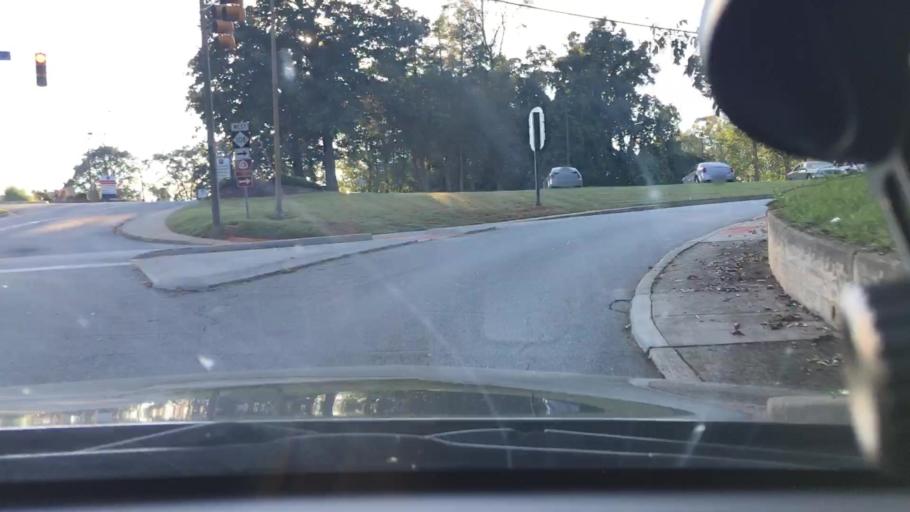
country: US
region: North Carolina
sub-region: Rutherford County
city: Rutherfordton
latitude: 35.3637
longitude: -81.9649
